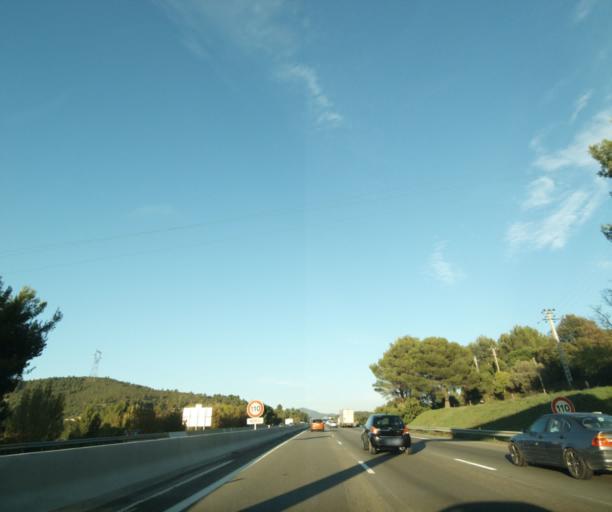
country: FR
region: Provence-Alpes-Cote d'Azur
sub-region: Departement des Bouches-du-Rhone
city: Roquevaire
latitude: 43.3447
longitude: 5.6132
